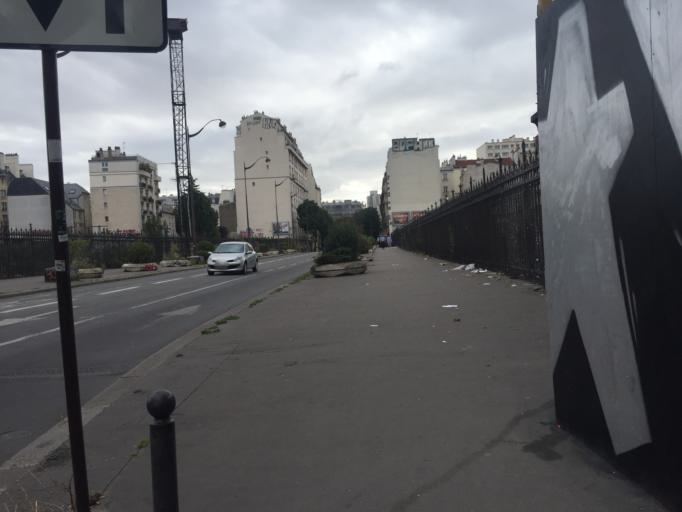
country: FR
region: Ile-de-France
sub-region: Paris
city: Saint-Ouen
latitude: 48.8903
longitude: 2.3562
